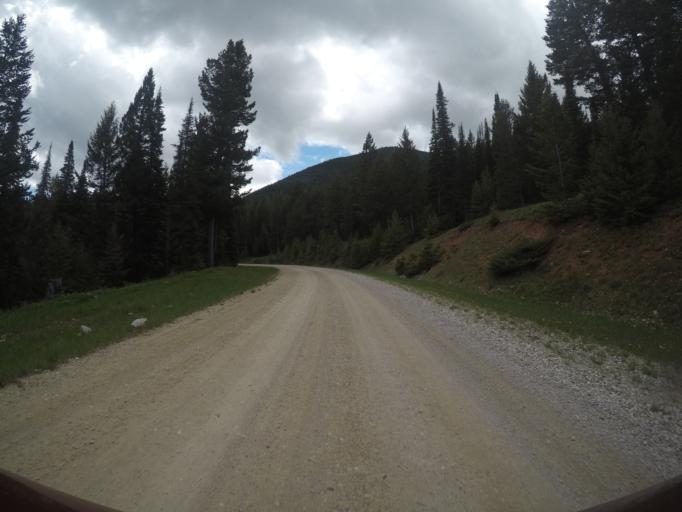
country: US
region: Wyoming
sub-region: Big Horn County
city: Lovell
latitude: 45.1767
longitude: -108.4640
